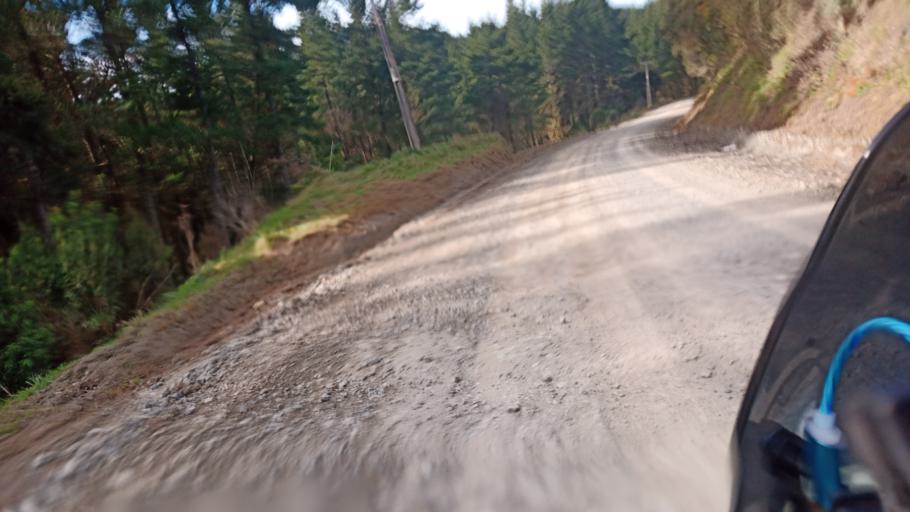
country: NZ
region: Gisborne
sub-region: Gisborne District
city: Gisborne
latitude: -38.1213
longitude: 178.1477
